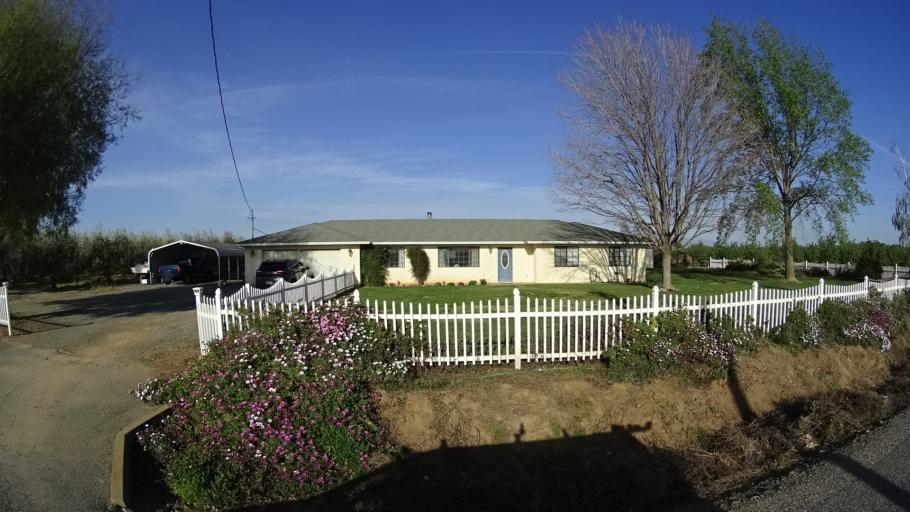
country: US
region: California
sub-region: Glenn County
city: Orland
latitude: 39.7222
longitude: -122.2347
